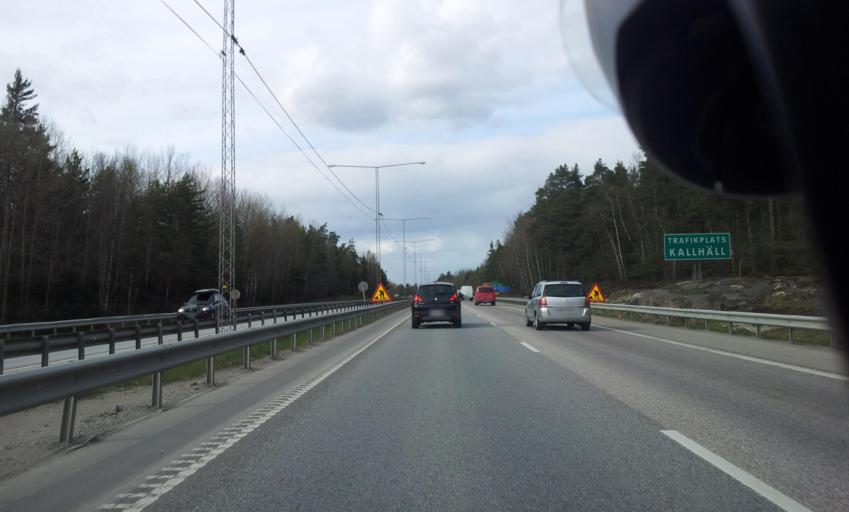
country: SE
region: Stockholm
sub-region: Jarfalla Kommun
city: Jakobsberg
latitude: 59.4403
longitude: 17.8429
